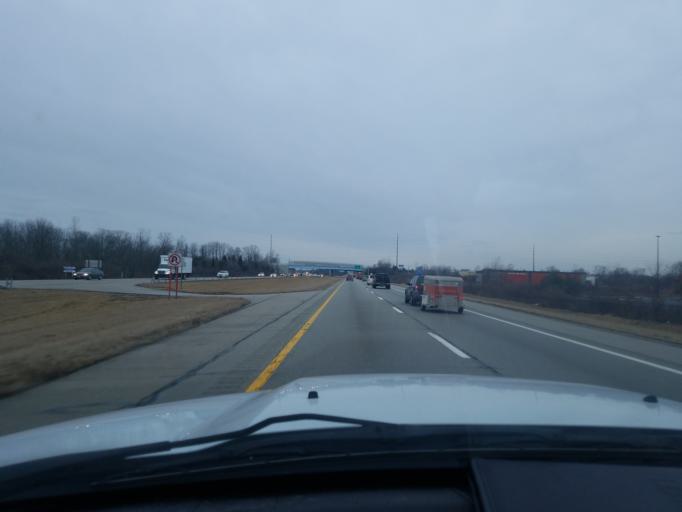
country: US
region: Ohio
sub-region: Montgomery County
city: Centerville
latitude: 39.6290
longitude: -84.2126
